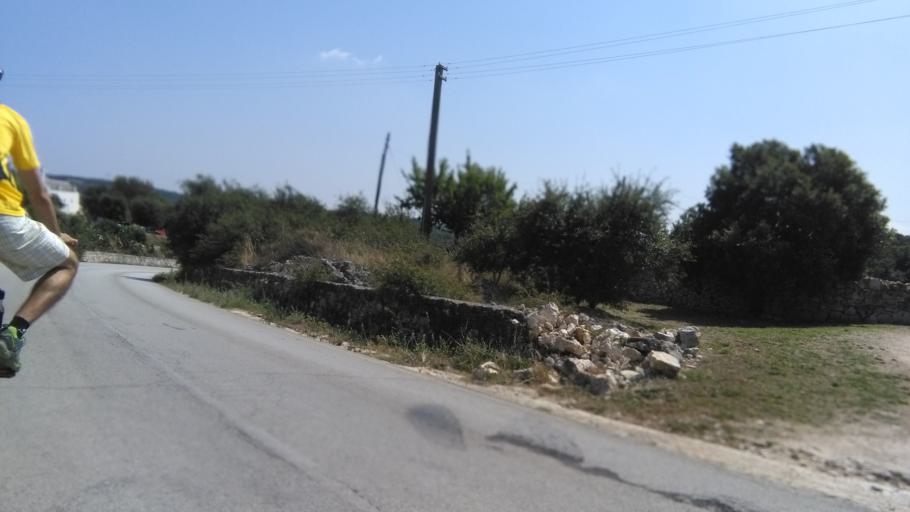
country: IT
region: Apulia
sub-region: Provincia di Bari
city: Alberobello
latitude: 40.8076
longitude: 17.1927
